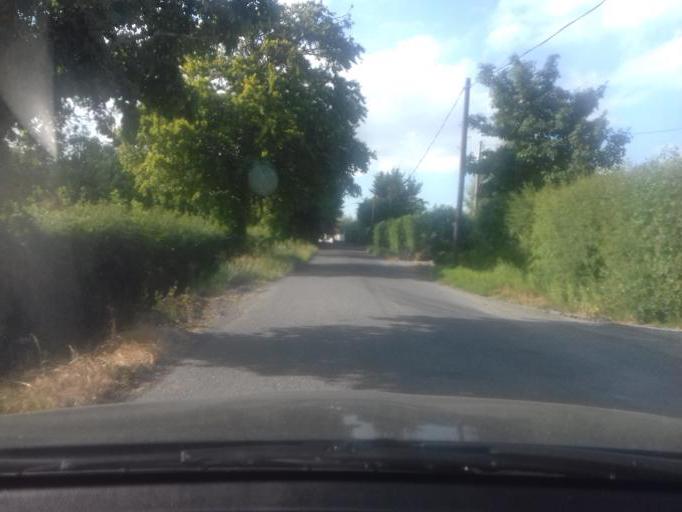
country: IE
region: Leinster
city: Hartstown
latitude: 53.4361
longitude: -6.4293
